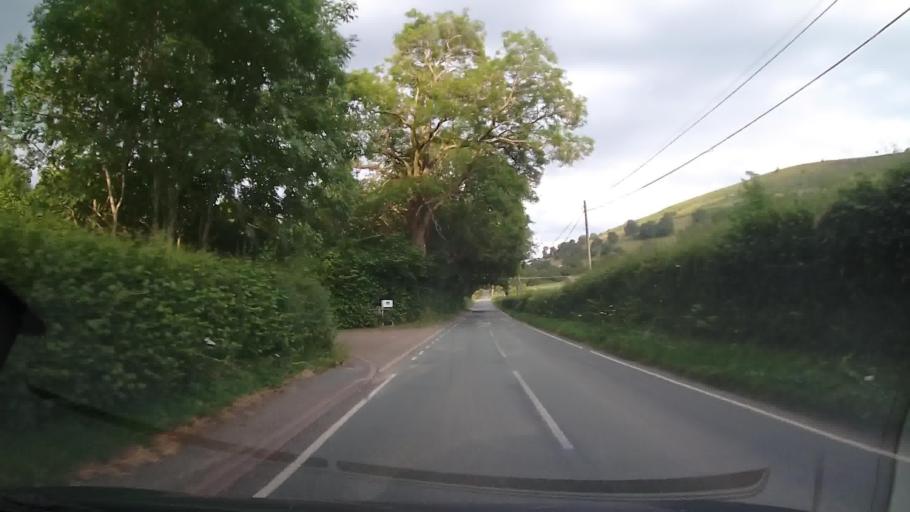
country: GB
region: Wales
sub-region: Sir Powys
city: Llanrhaeadr-ym-Mochnant
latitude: 52.8109
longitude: -3.3497
